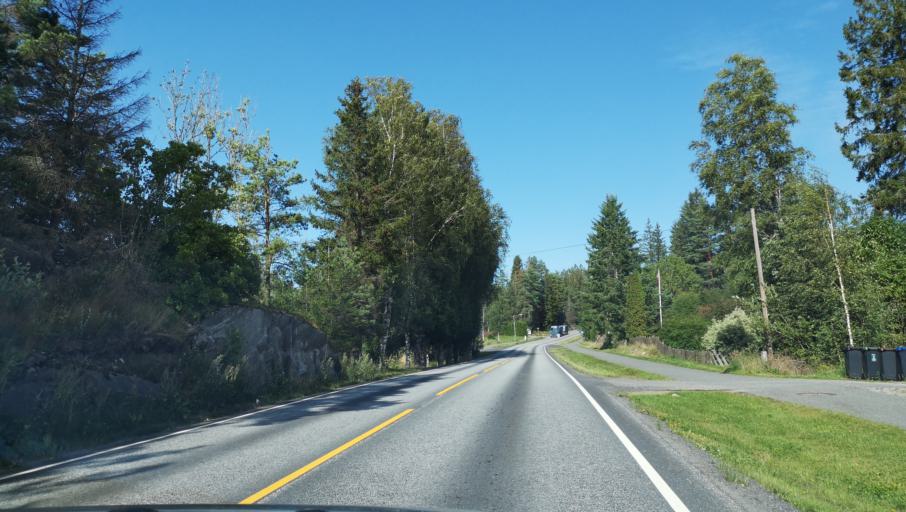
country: NO
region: Ostfold
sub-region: Valer
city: Kirkebygda
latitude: 59.5662
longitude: 10.8562
